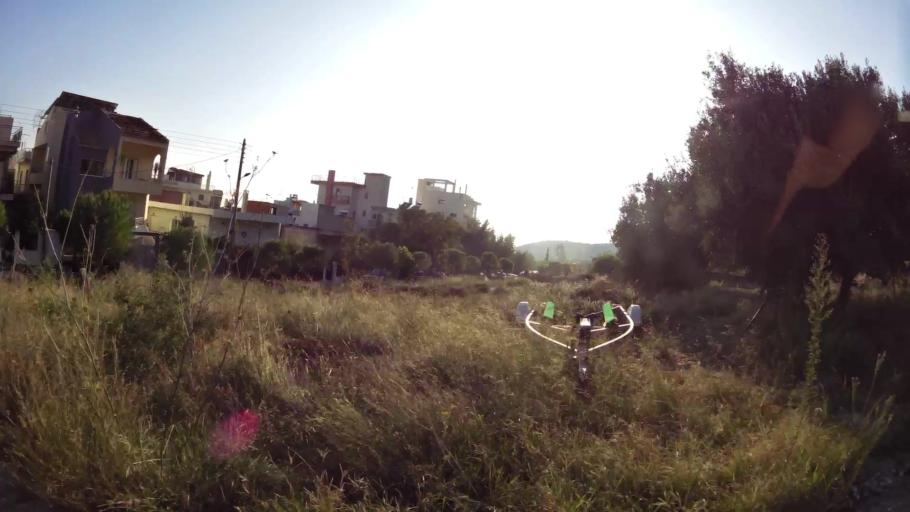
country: GR
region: Attica
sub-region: Nomarchia Athinas
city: Argyroupoli
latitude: 37.9036
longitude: 23.7705
